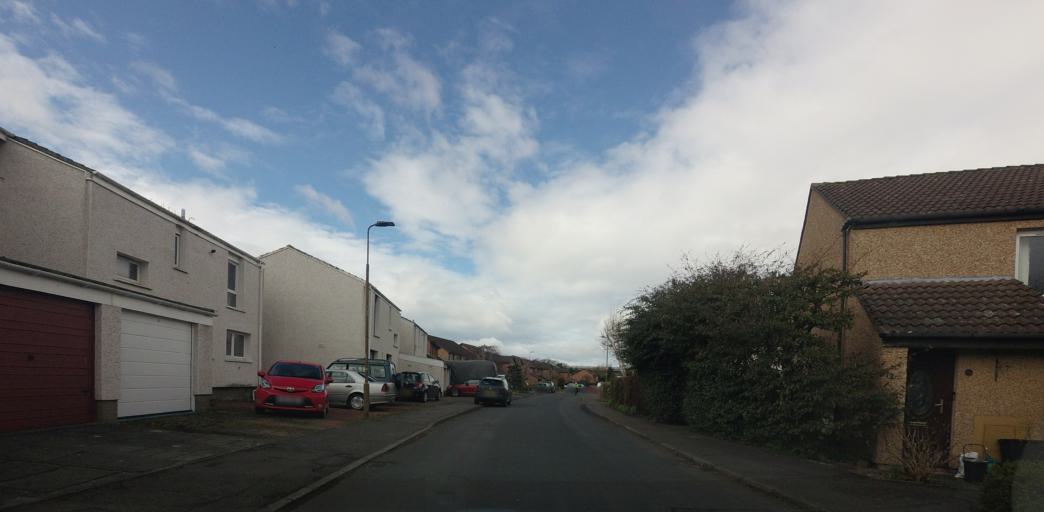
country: GB
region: Scotland
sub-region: Edinburgh
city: Queensferry
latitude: 55.9911
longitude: -3.4134
